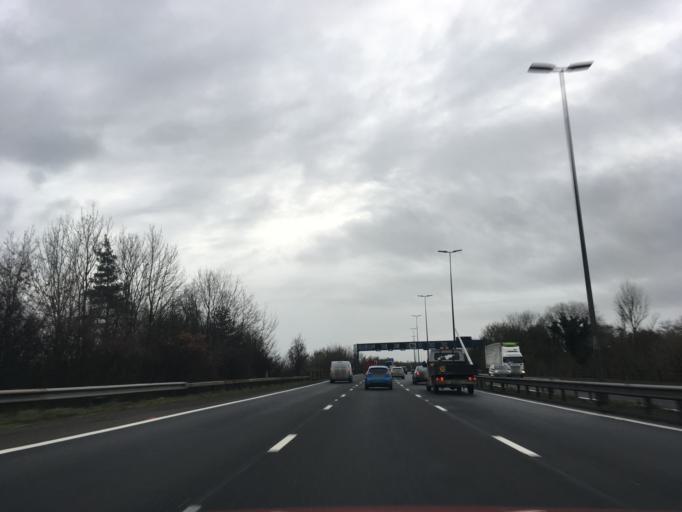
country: GB
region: Wales
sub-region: Newport
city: Newport
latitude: 51.5692
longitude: -3.0342
